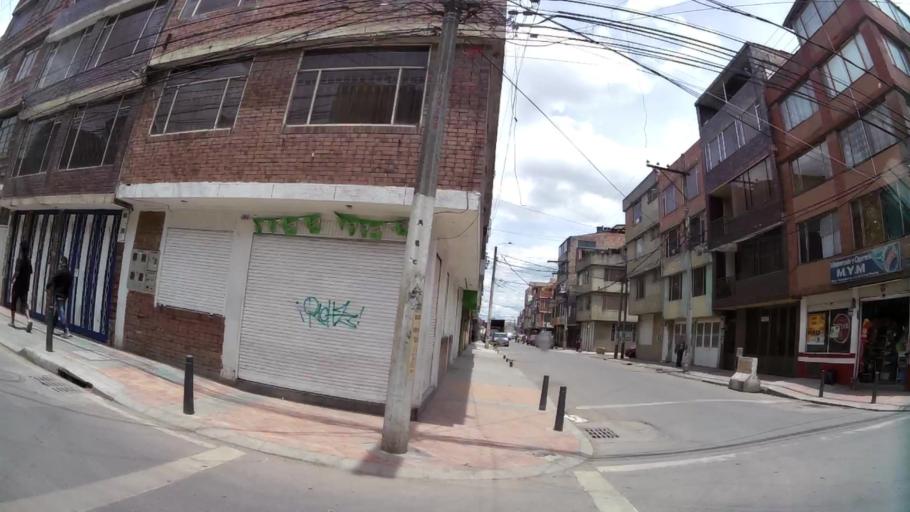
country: CO
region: Bogota D.C.
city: Bogota
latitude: 4.6451
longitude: -74.1483
